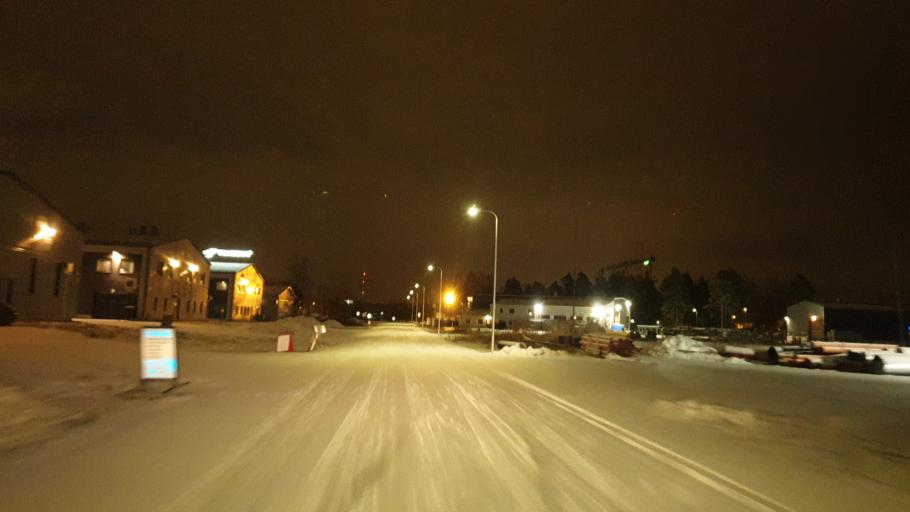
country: FI
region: Northern Ostrobothnia
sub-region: Oulu
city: Oulu
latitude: 64.9946
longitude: 25.4443
